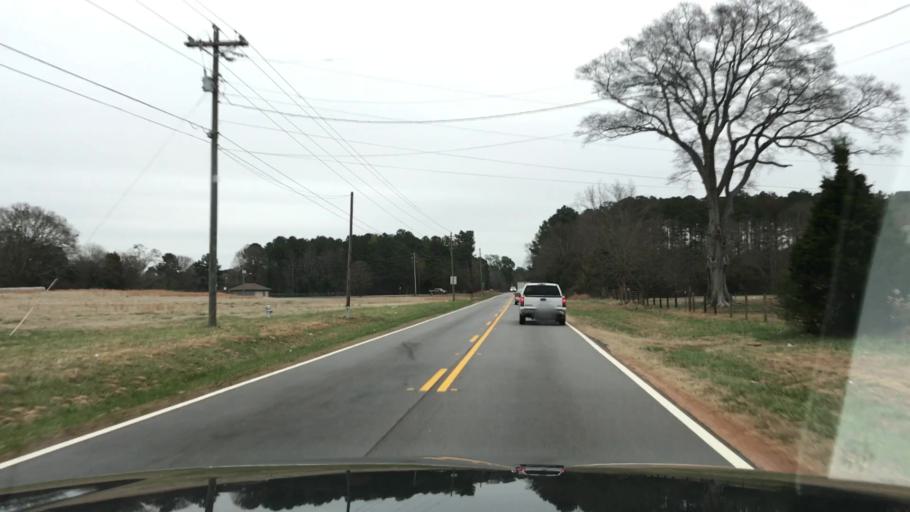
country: US
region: Georgia
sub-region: Walton County
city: Monroe
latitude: 33.8607
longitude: -83.7433
